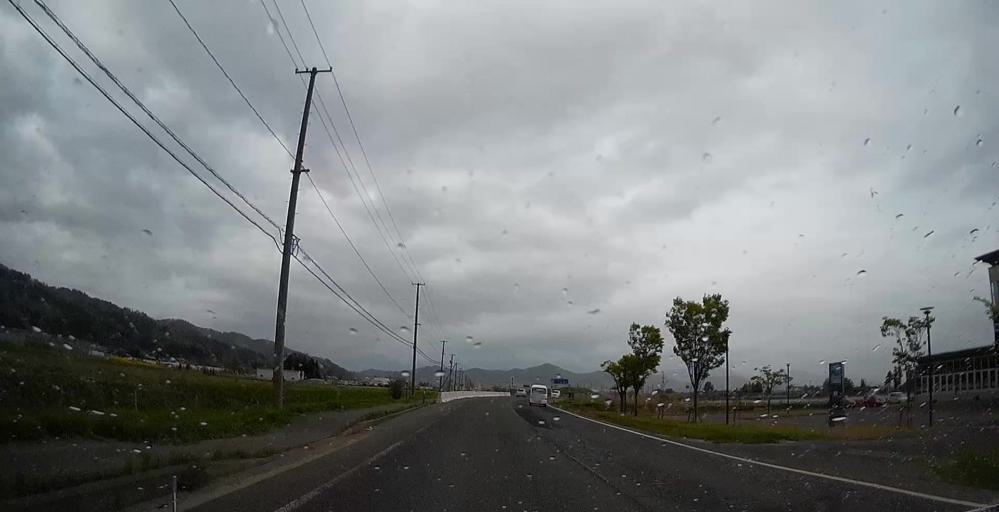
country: JP
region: Yamagata
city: Nagai
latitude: 38.0575
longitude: 140.1055
